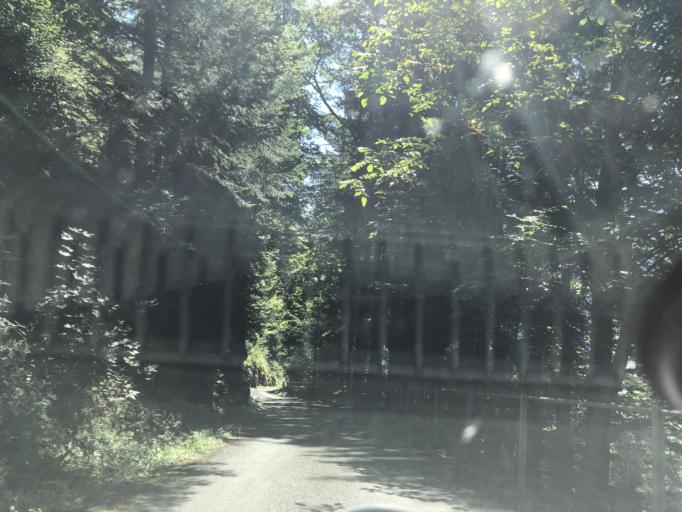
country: CH
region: Uri
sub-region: Uri
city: Flueelen
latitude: 46.9071
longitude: 8.6338
